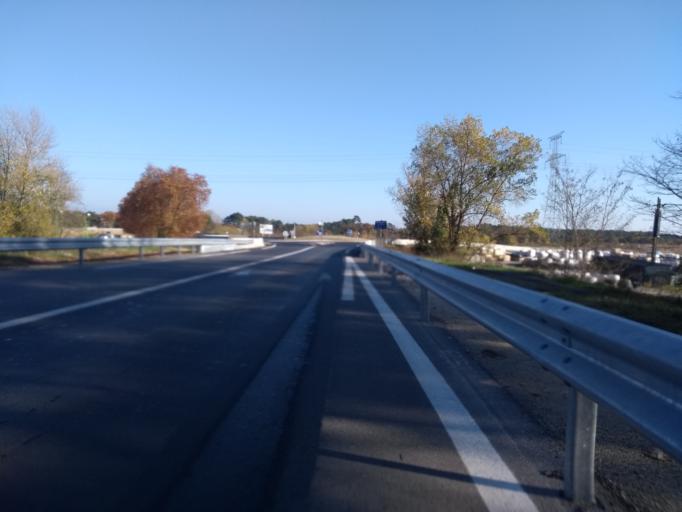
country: FR
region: Aquitaine
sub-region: Departement de la Gironde
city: Ayguemorte-les-Graves
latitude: 44.6926
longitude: -0.5022
